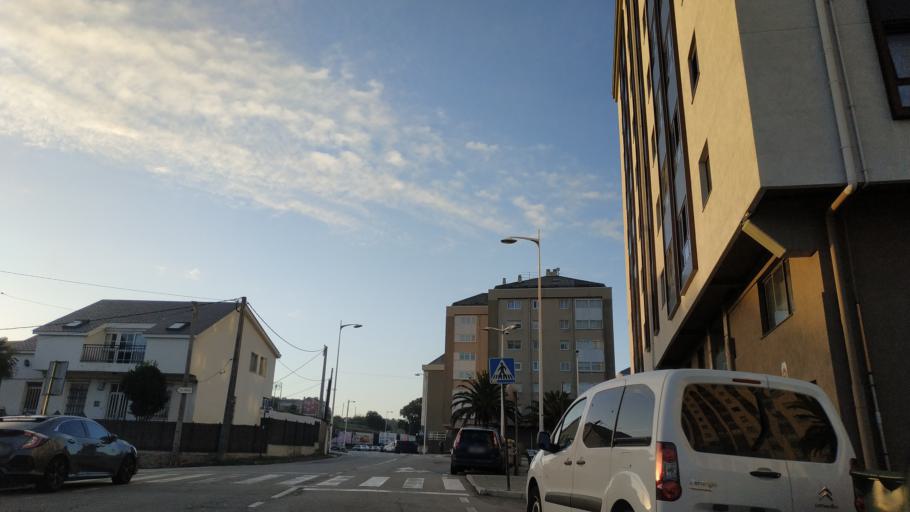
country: ES
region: Galicia
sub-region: Provincia da Coruna
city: A Coruna
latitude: 43.3583
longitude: -8.4249
